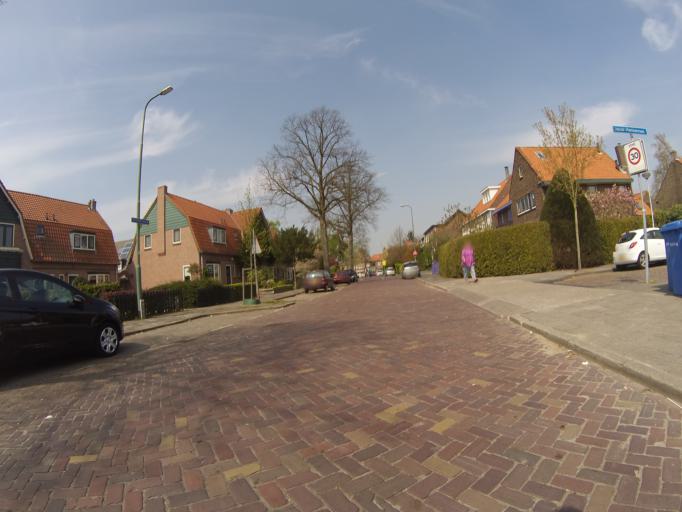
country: NL
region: Utrecht
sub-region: Gemeente Amersfoort
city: Amersfoort
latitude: 52.1470
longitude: 5.3887
